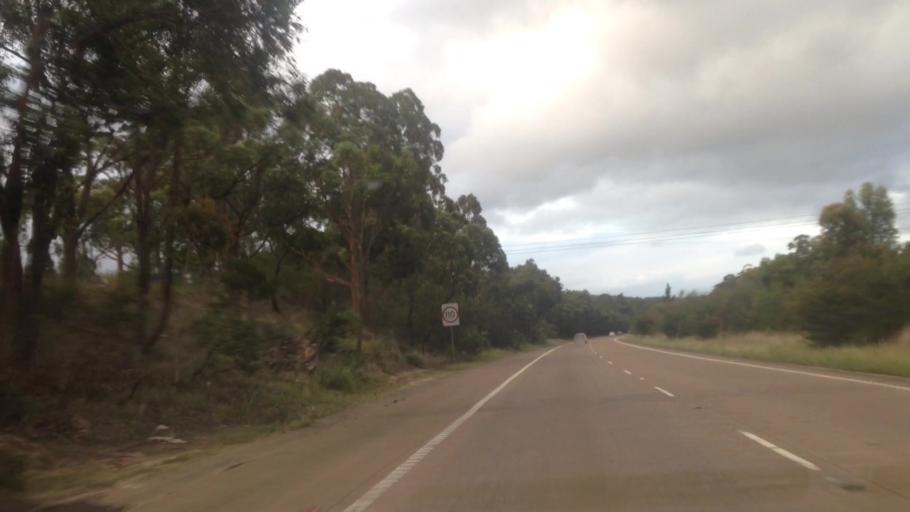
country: AU
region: New South Wales
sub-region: Wyong Shire
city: Charmhaven
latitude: -33.1751
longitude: 151.4667
